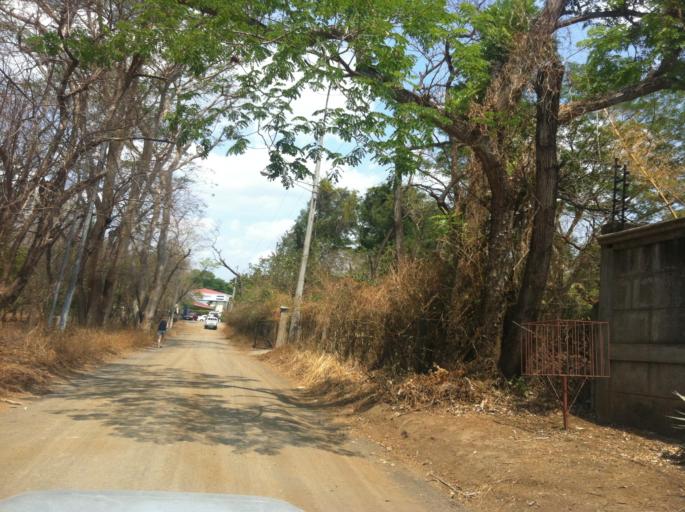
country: NI
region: Managua
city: Ciudad Sandino
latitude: 12.0873
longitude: -86.3309
